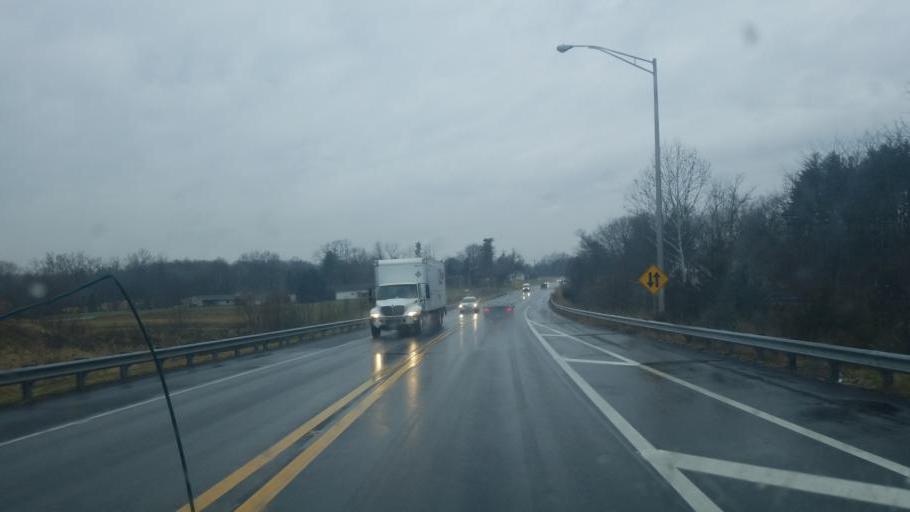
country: US
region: Indiana
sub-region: Bartholomew County
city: Columbus
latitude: 39.1995
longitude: -85.9752
